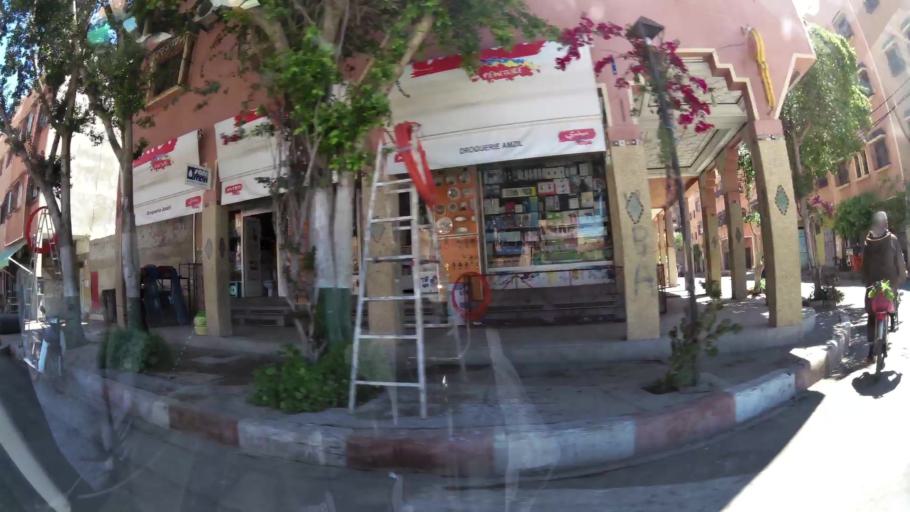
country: MA
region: Marrakech-Tensift-Al Haouz
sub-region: Marrakech
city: Marrakesh
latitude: 31.6305
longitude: -8.0666
